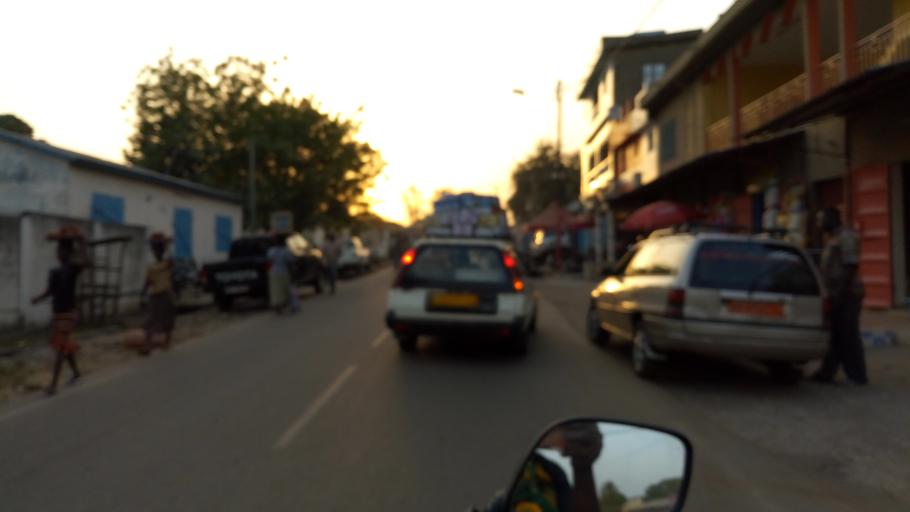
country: TG
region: Kara
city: Kara
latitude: 9.5485
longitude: 1.1919
